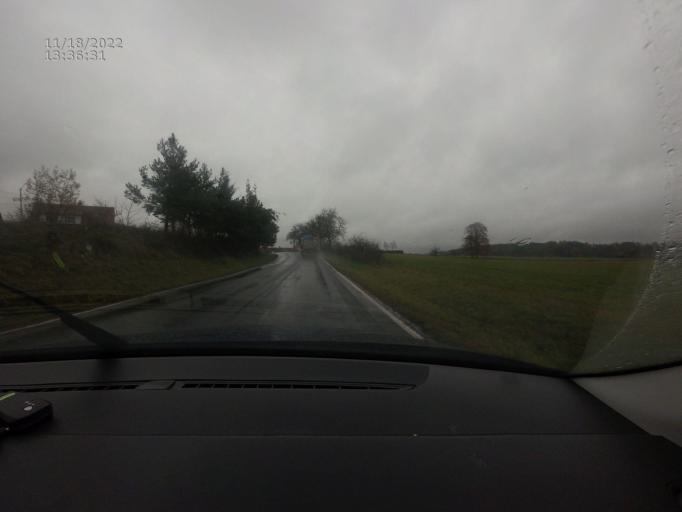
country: CZ
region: Plzensky
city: Kasejovice
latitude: 49.4143
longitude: 13.7831
